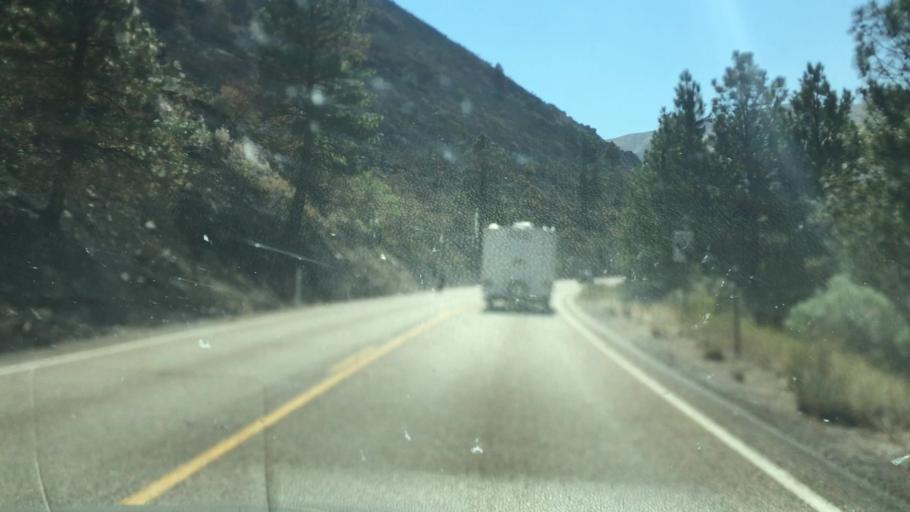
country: US
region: Idaho
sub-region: Gem County
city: Emmett
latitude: 44.0087
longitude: -116.1664
